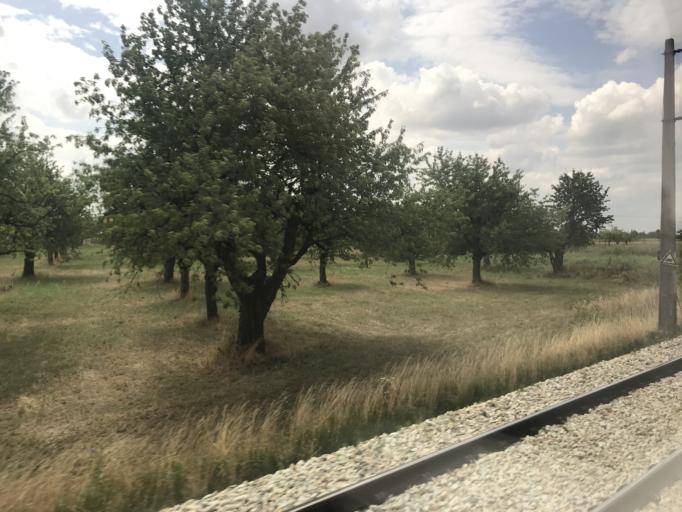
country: PL
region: Greater Poland Voivodeship
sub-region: Powiat poznanski
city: Buk
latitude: 52.3471
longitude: 16.5470
